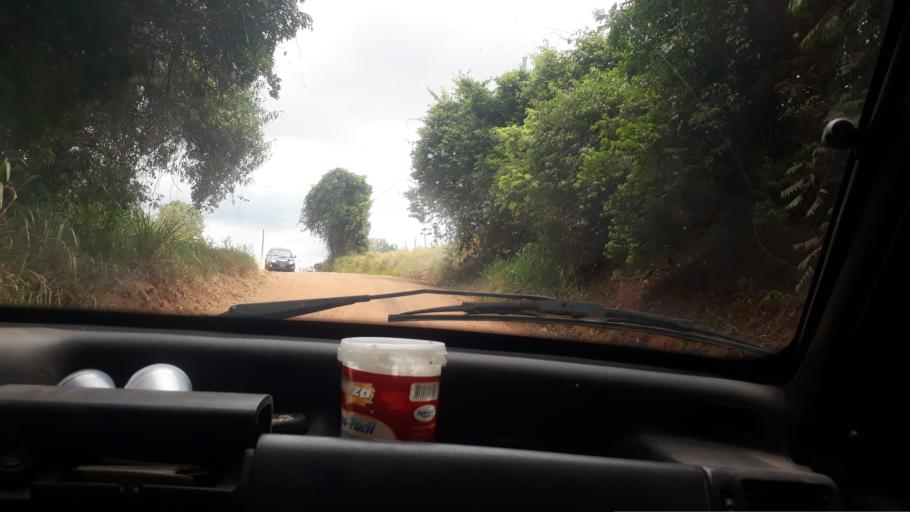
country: BR
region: Sao Paulo
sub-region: Regente Feijo
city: Regente Feijo
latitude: -22.2412
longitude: -51.2980
